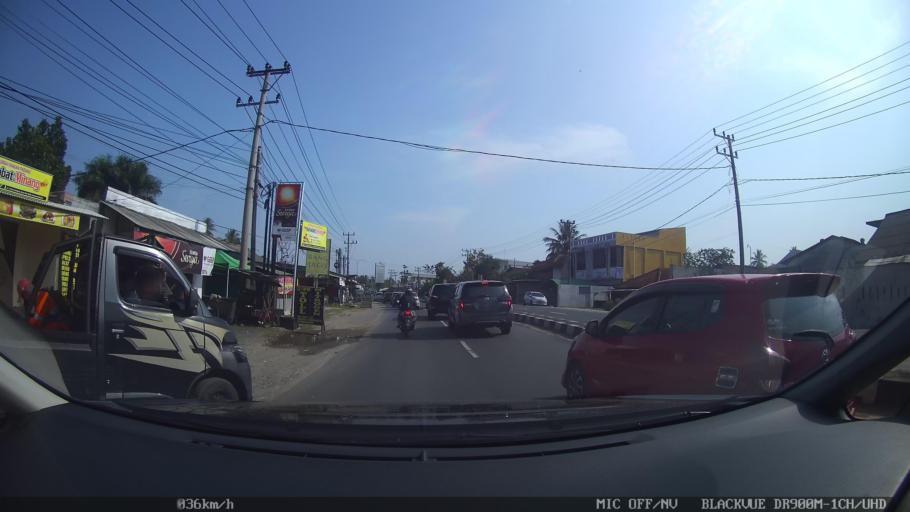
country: ID
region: Lampung
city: Natar
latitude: -5.2849
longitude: 105.1910
